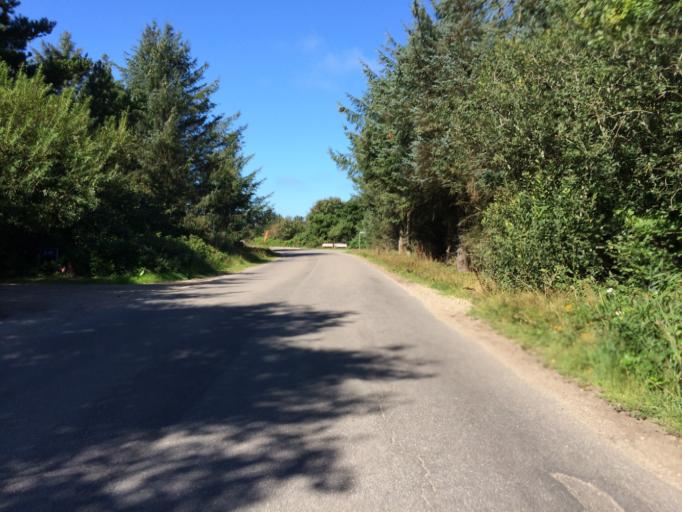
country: DK
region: Central Jutland
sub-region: Holstebro Kommune
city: Ulfborg
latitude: 56.2596
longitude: 8.1481
